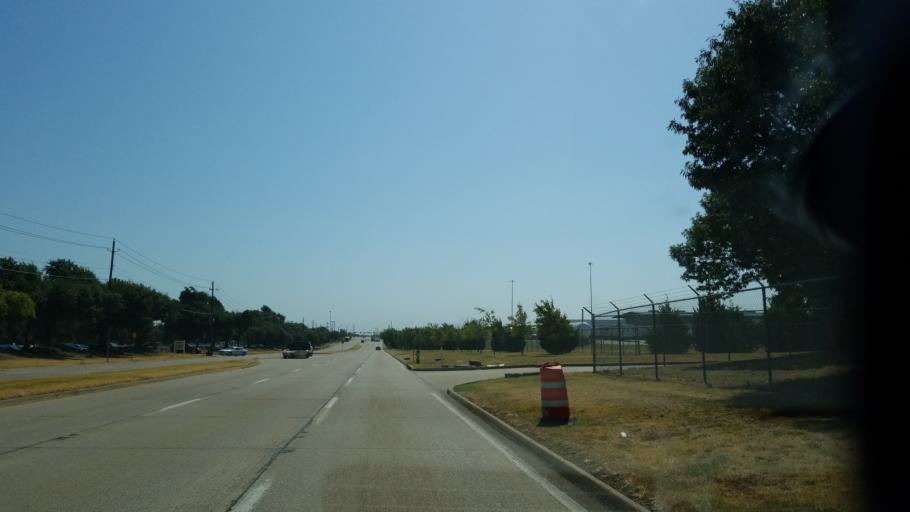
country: US
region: Texas
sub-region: Dallas County
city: Cockrell Hill
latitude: 32.7056
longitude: -96.9136
